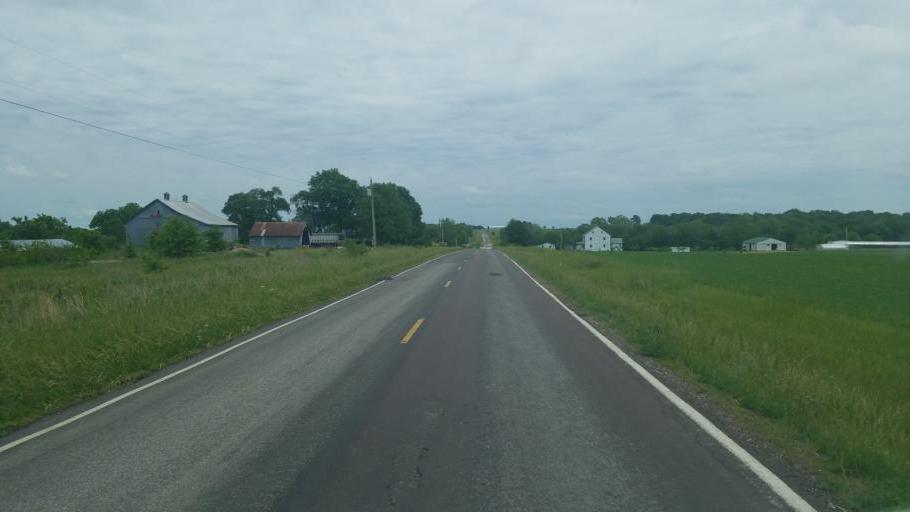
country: US
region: Missouri
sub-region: Morgan County
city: Versailles
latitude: 38.5107
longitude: -92.7603
